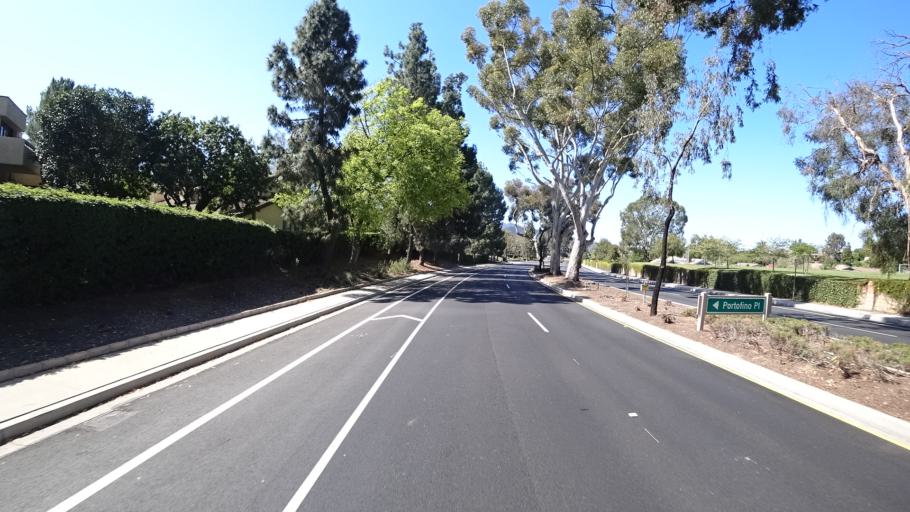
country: US
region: California
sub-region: Ventura County
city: Casa Conejo
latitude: 34.1967
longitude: -118.8905
